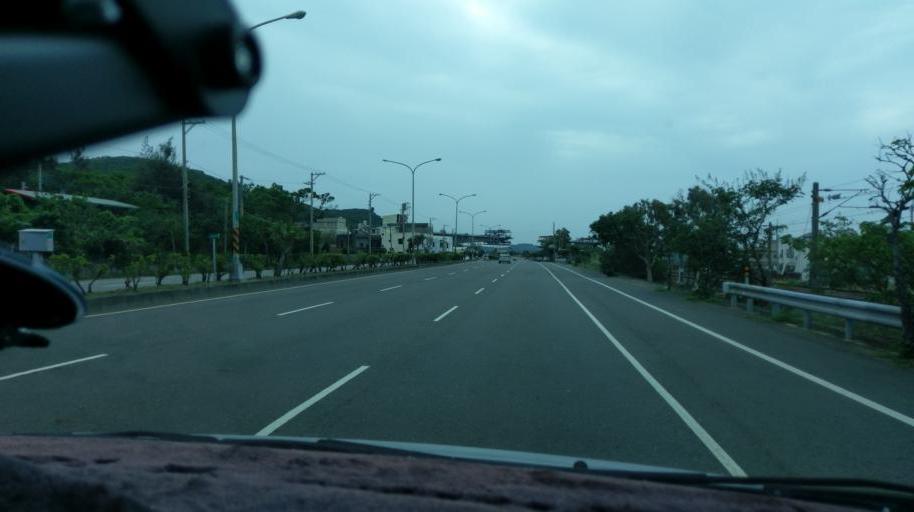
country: TW
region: Taiwan
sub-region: Miaoli
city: Miaoli
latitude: 24.5347
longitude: 120.6942
